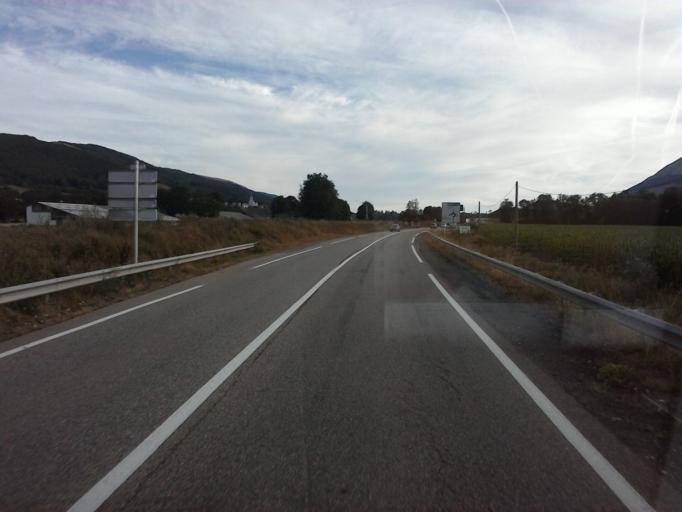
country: FR
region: Rhone-Alpes
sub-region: Departement de l'Isere
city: Pierre-Chatel
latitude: 44.9459
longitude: 5.7796
